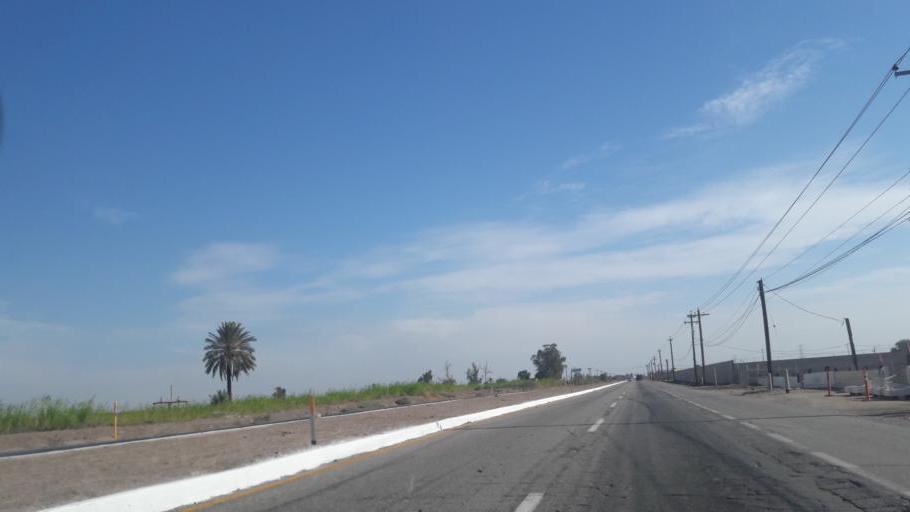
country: MX
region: Baja California
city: Progreso
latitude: 32.5879
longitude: -115.6060
